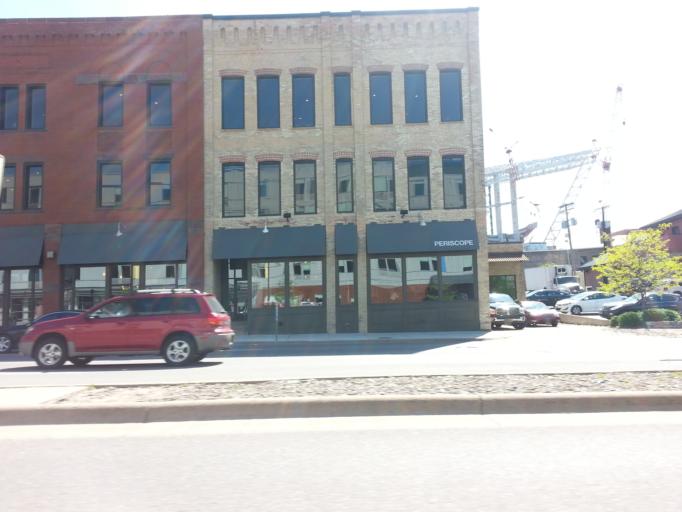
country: US
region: Minnesota
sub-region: Hennepin County
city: Minneapolis
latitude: 44.9764
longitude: -93.2551
